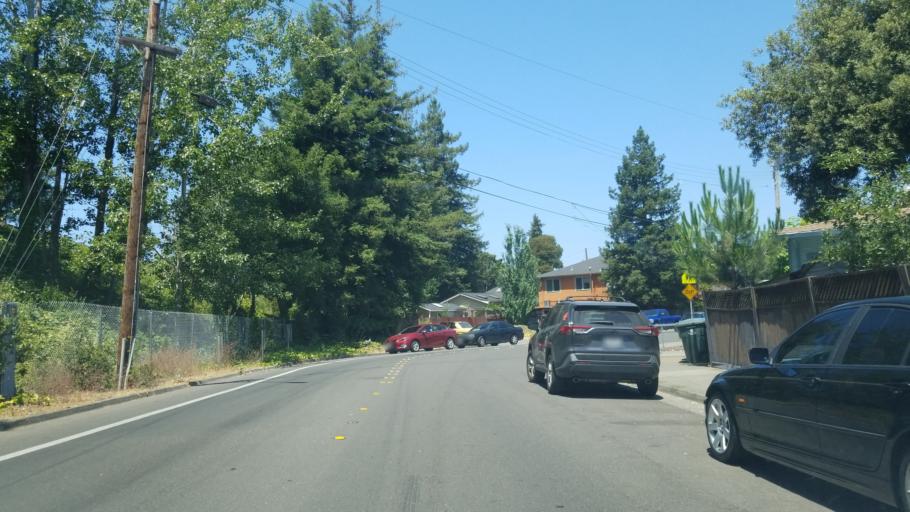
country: US
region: California
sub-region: Sonoma County
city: Santa Rosa
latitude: 38.4323
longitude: -122.7145
